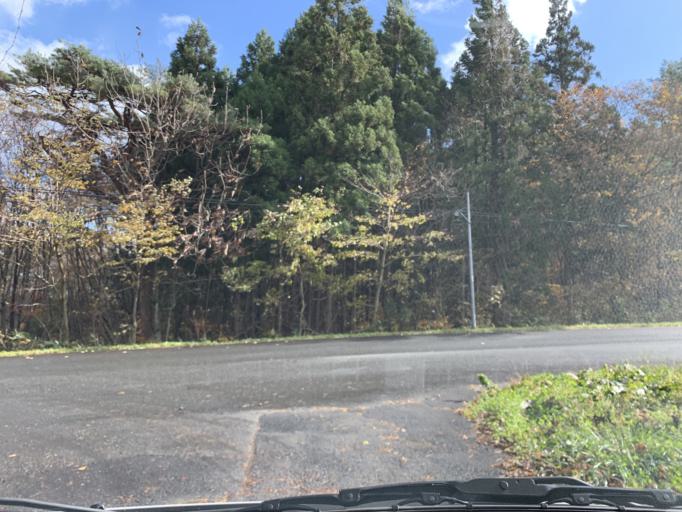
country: JP
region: Iwate
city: Mizusawa
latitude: 39.1014
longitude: 140.9864
